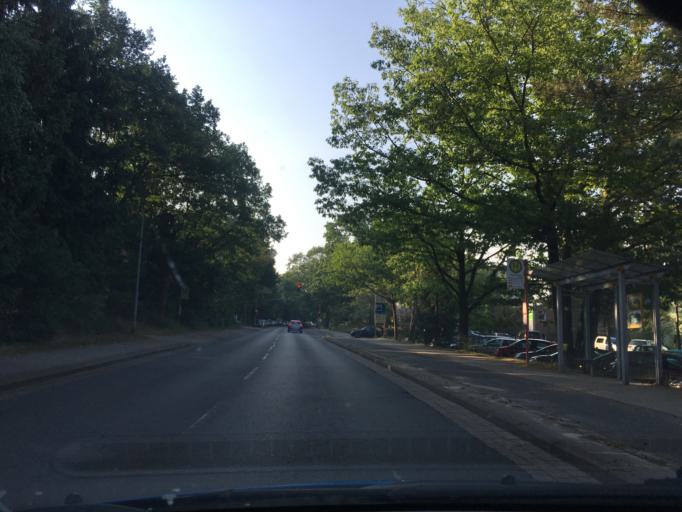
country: DE
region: Lower Saxony
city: Buchholz in der Nordheide
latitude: 53.3357
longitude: 9.8713
